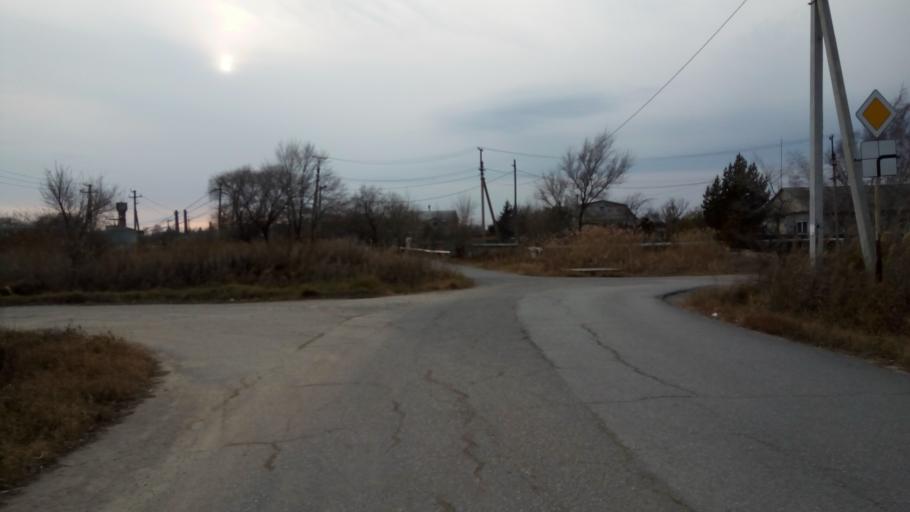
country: RU
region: Primorskiy
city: Novoshakhtinskiy
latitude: 44.0225
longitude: 132.1634
